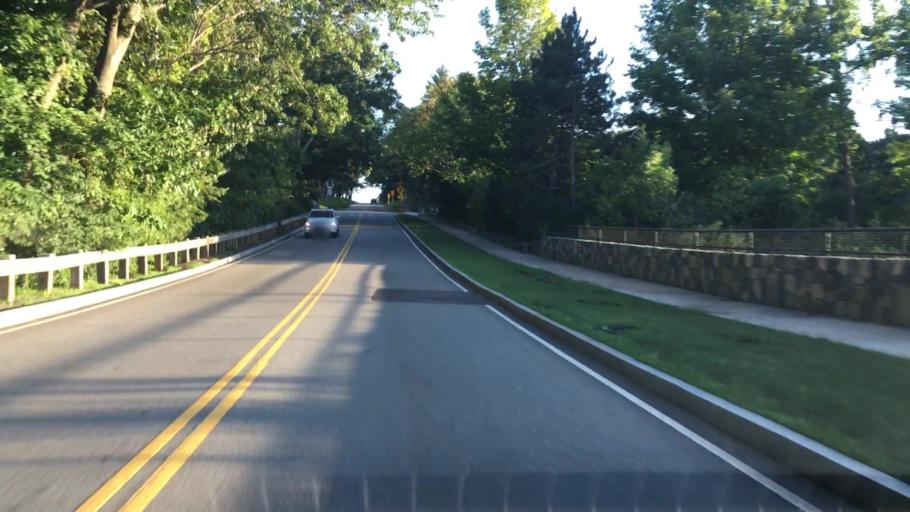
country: US
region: Massachusetts
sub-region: Middlesex County
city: Waltham
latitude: 42.4079
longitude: -71.2562
